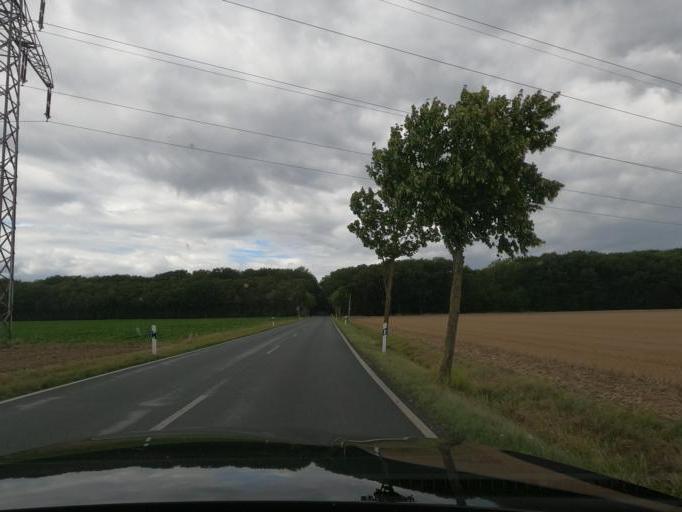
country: DE
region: Lower Saxony
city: Sehnde
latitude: 52.3035
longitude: 9.8981
